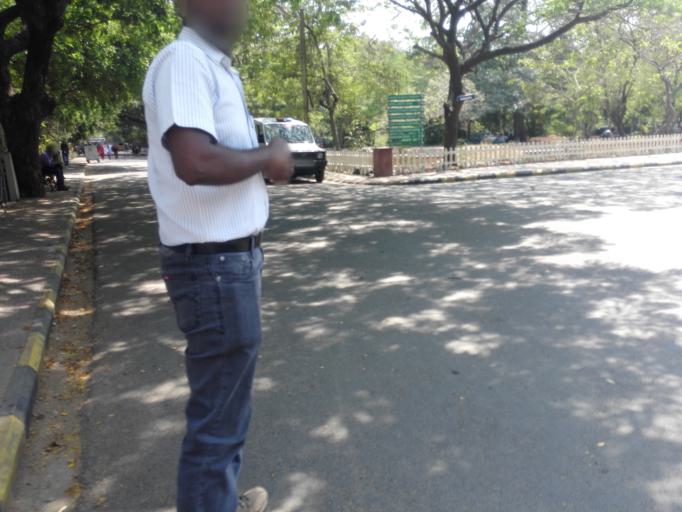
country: IN
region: Tamil Nadu
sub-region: Chennai
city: Gandhi Nagar
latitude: 13.0107
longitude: 80.2364
